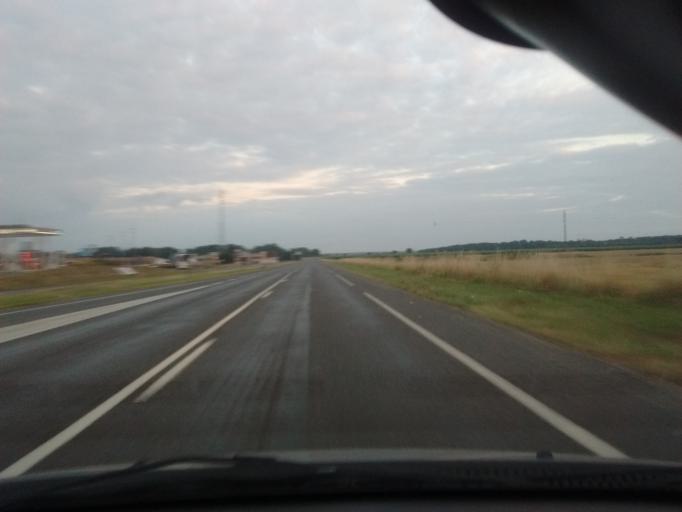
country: FR
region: Ile-de-France
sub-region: Departement de Seine-et-Marne
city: Pringy
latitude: 48.5014
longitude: 2.5781
